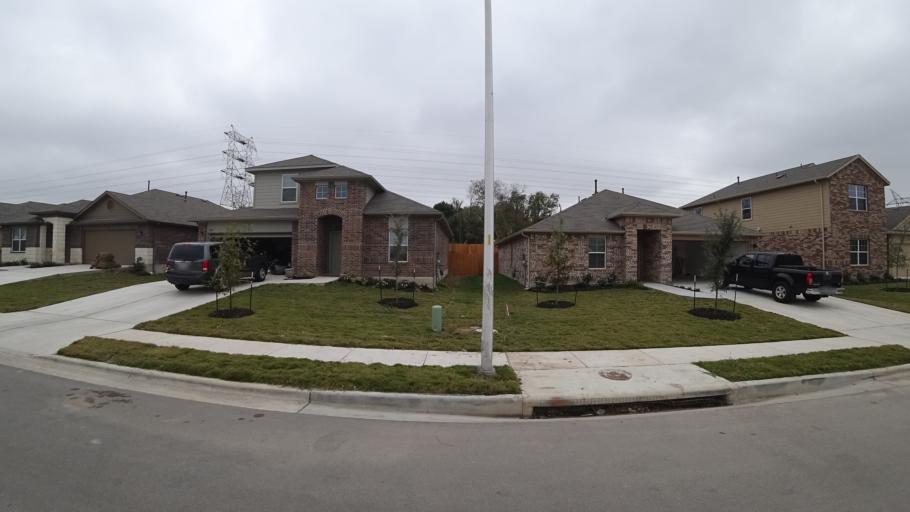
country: US
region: Texas
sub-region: Travis County
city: Pflugerville
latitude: 30.3682
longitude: -97.6484
